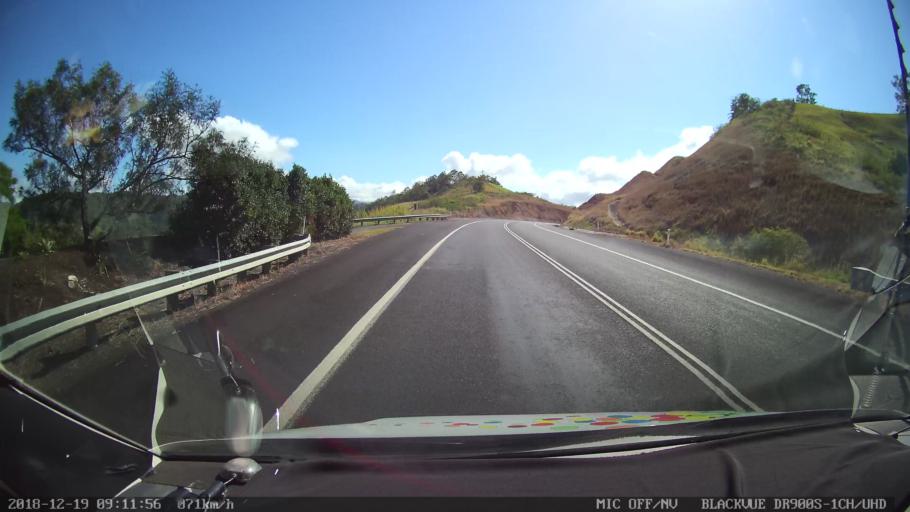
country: AU
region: New South Wales
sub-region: Kyogle
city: Kyogle
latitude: -28.4953
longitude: 152.9439
